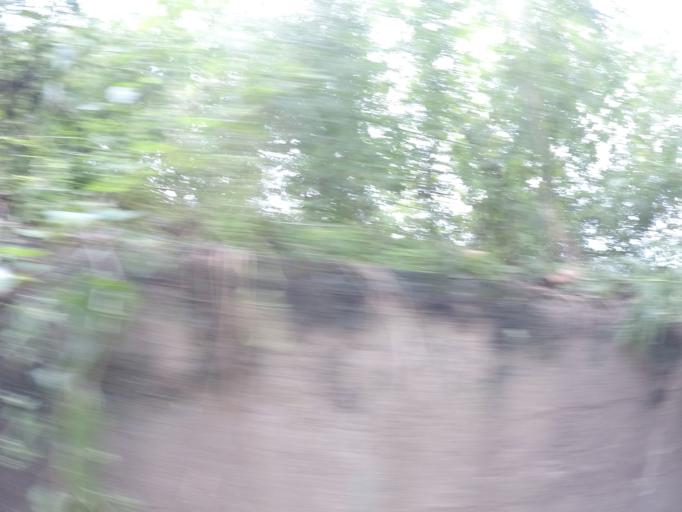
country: US
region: West Virginia
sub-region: Cabell County
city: Huntington
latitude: 38.4206
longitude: -82.3897
